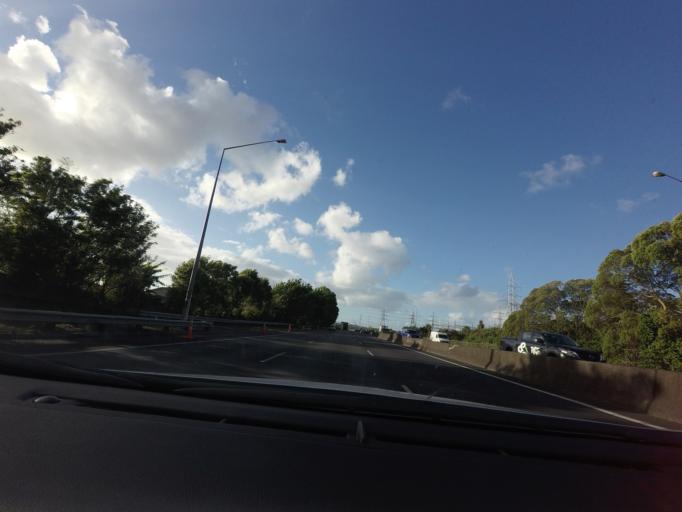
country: NZ
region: Auckland
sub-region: Auckland
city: Wiri
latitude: -36.9579
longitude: 174.8596
